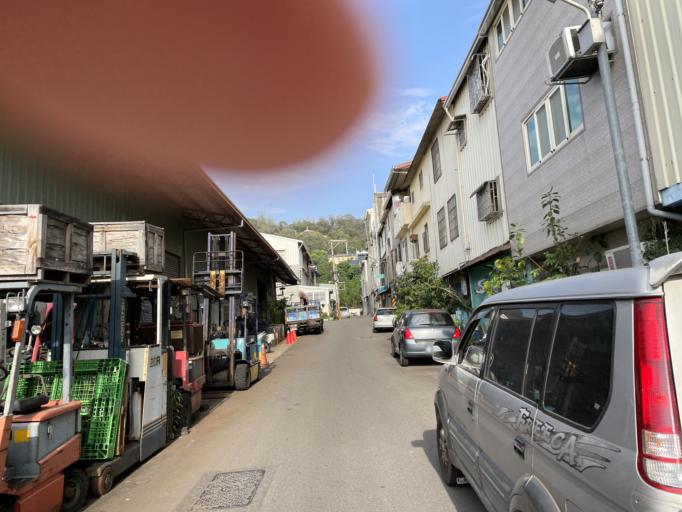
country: TW
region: Taiwan
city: Fengyuan
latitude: 24.2161
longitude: 120.7288
